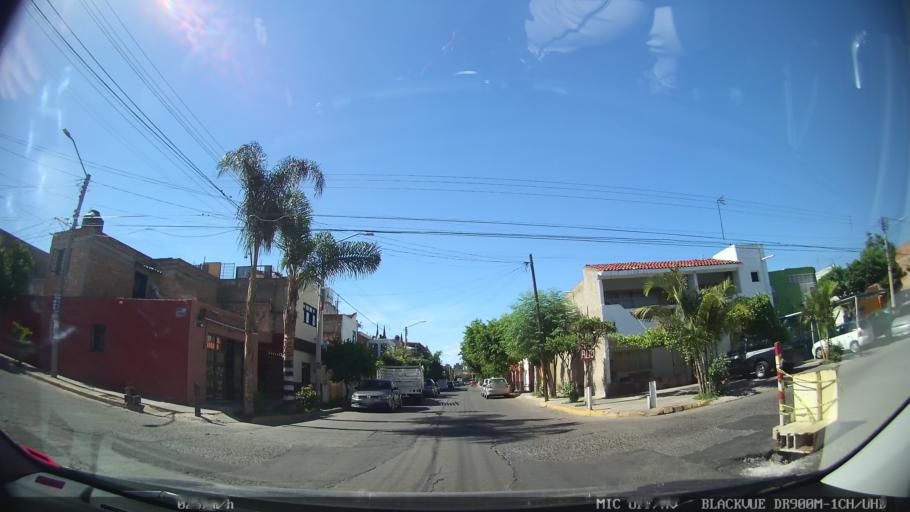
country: MX
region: Jalisco
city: Tlaquepaque
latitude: 20.6578
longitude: -103.2828
